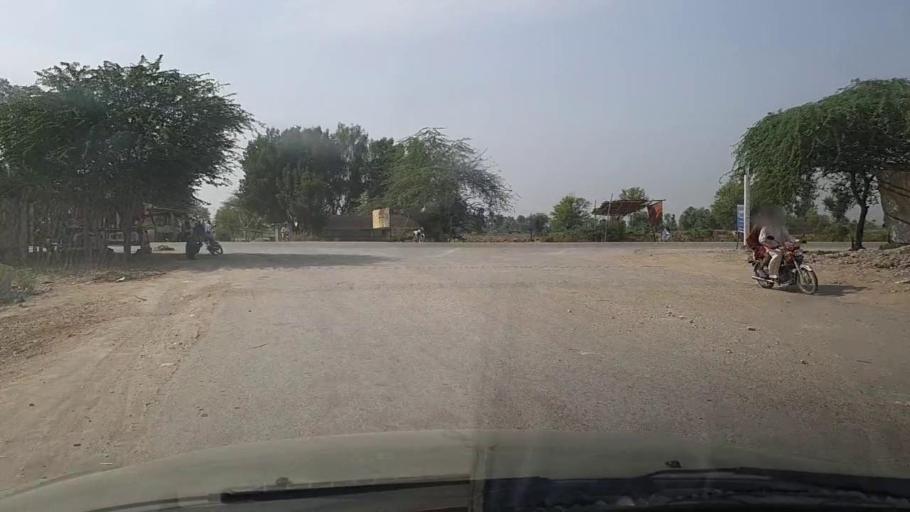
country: PK
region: Sindh
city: Gambat
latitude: 27.4413
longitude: 68.4861
